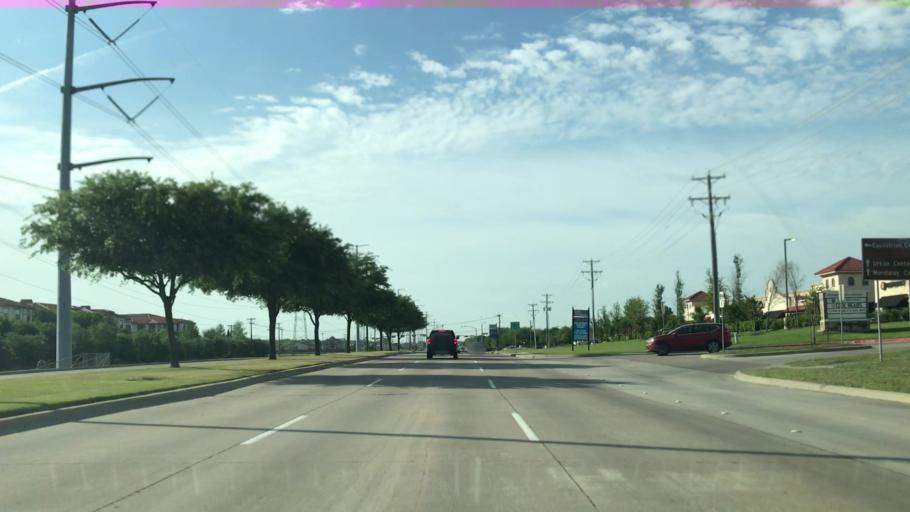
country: US
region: Texas
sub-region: Dallas County
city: Farmers Branch
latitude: 32.8982
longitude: -96.9395
